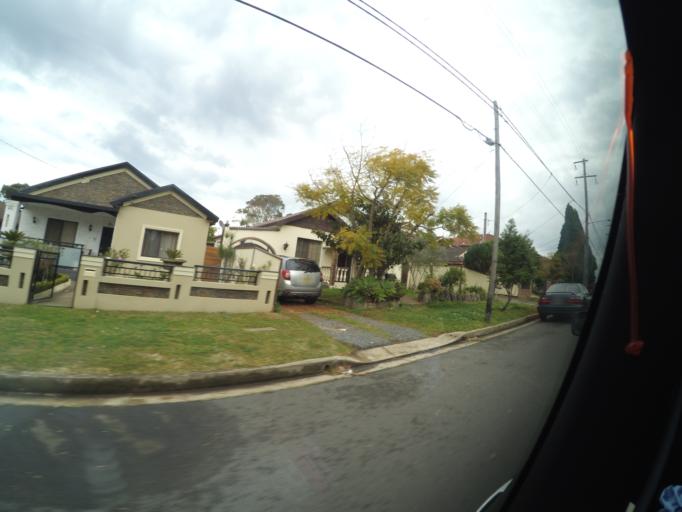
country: AU
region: New South Wales
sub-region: Bankstown
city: Bankstown
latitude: -33.9278
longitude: 151.0283
